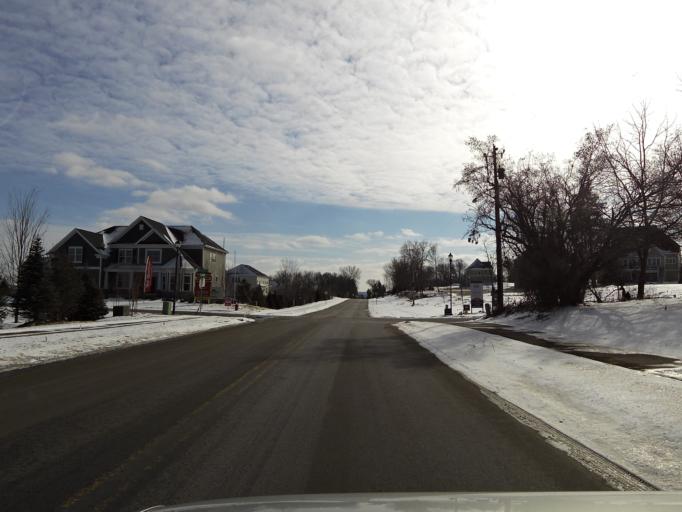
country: US
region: Minnesota
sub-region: Hennepin County
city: Eden Prairie
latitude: 44.8246
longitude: -93.4853
